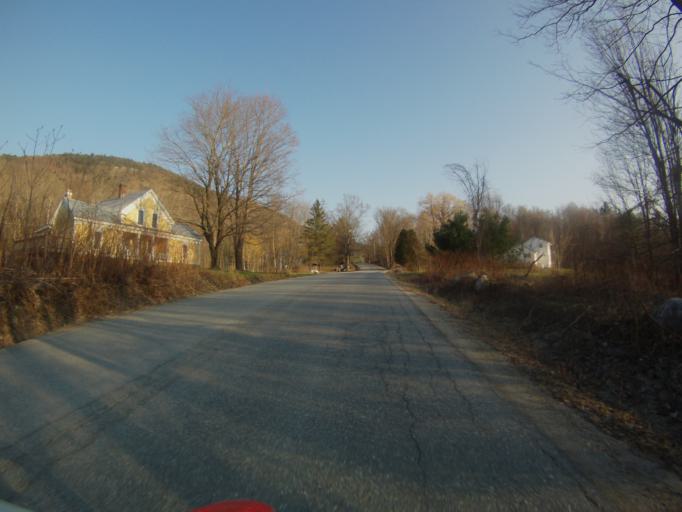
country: US
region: Vermont
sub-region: Addison County
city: Bristol
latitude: 44.1210
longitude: -73.0814
